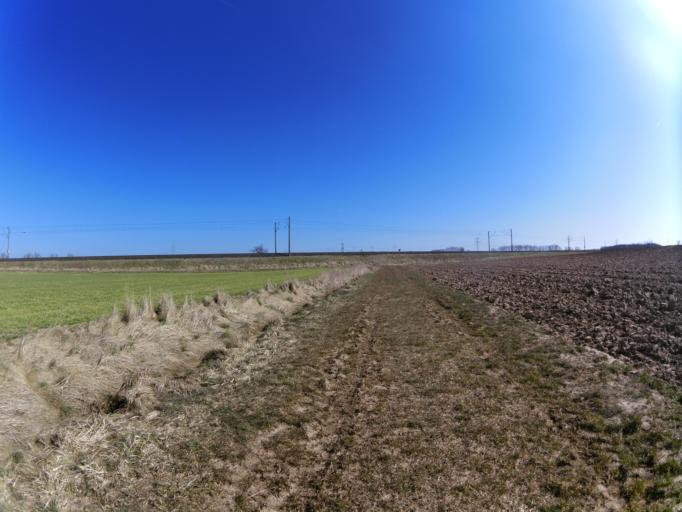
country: DE
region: Bavaria
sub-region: Regierungsbezirk Unterfranken
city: Oberpleichfeld
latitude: 49.8915
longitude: 10.0802
